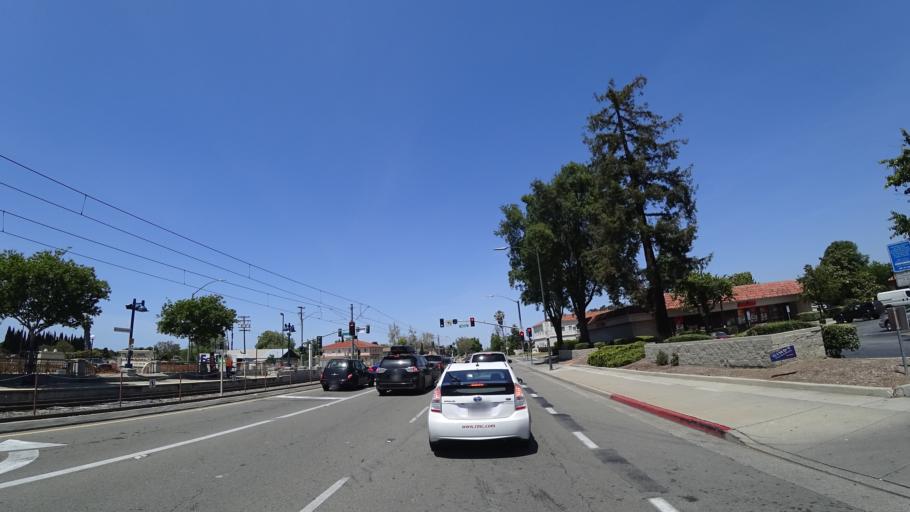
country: US
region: California
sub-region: Santa Clara County
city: Alum Rock
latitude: 37.3878
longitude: -121.8617
